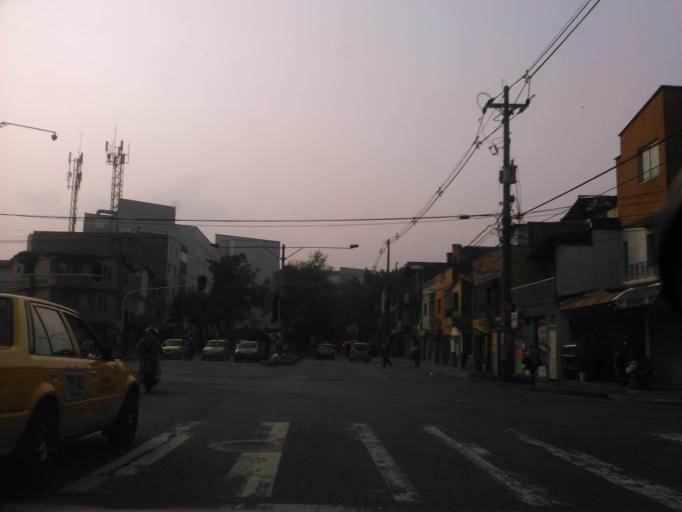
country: CO
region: Antioquia
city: Itagui
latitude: 6.2261
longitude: -75.6008
